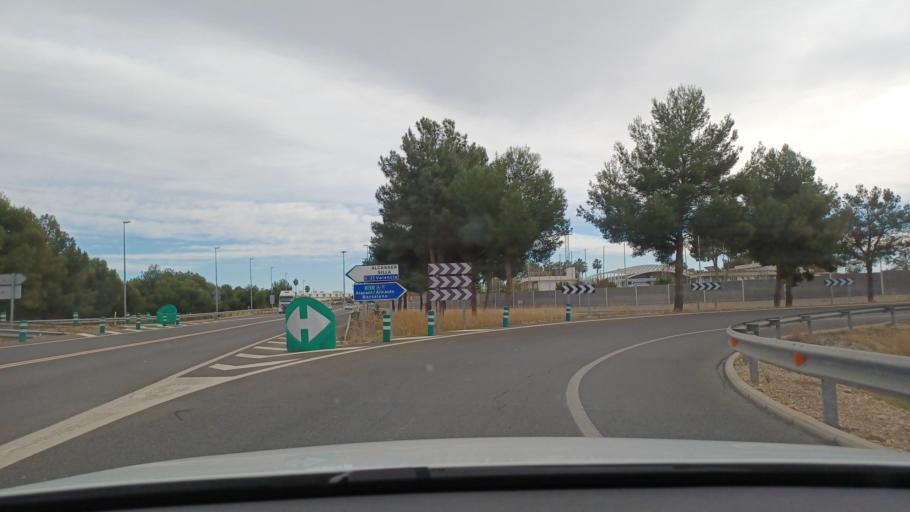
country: ES
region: Valencia
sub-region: Provincia de Valencia
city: Picassent
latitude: 39.3682
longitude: -0.4554
